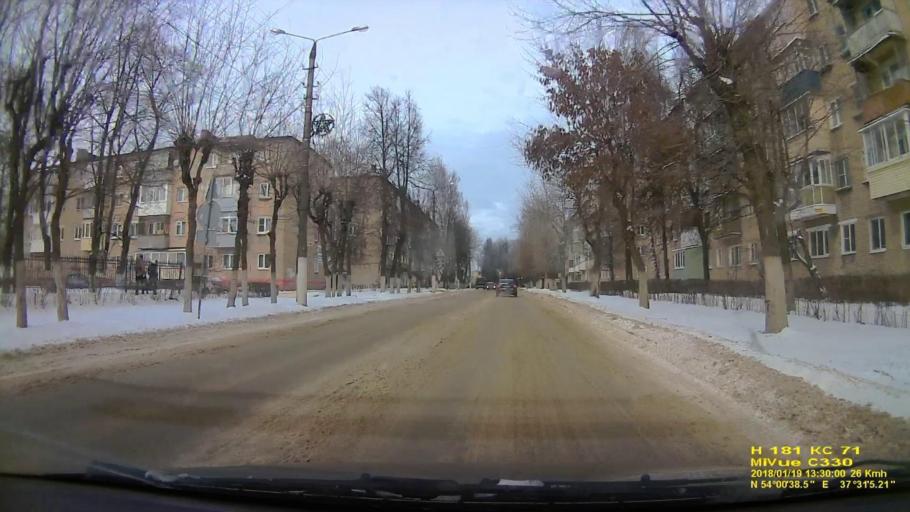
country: RU
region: Tula
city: Shchekino
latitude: 54.0108
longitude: 37.5181
